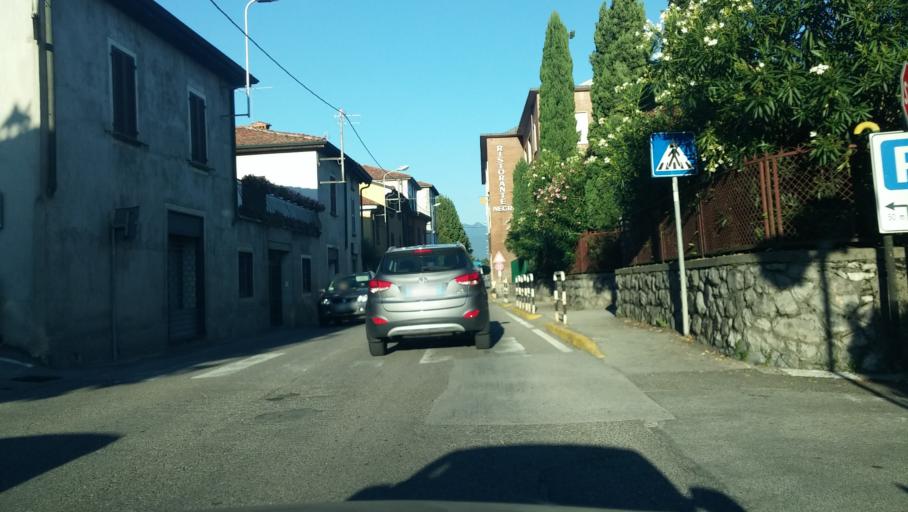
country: IT
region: Lombardy
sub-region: Provincia di Como
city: Pusiano
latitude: 45.8134
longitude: 9.2814
